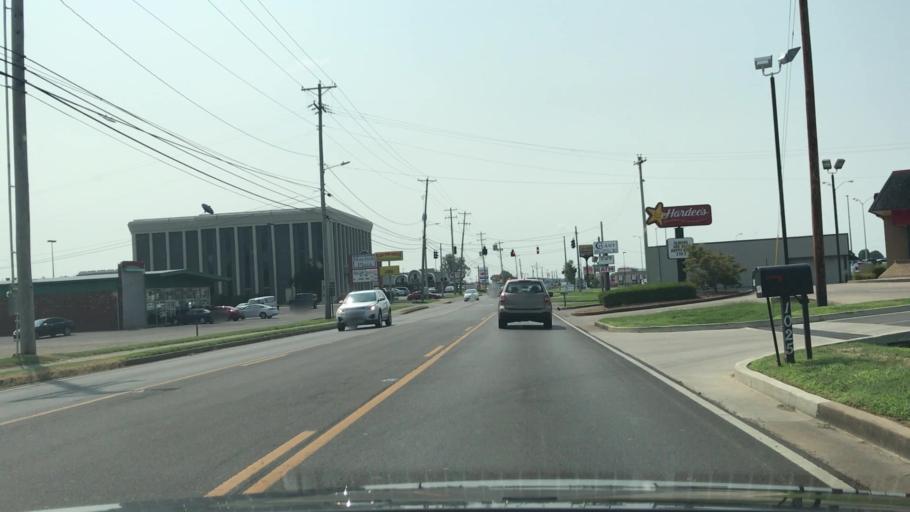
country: US
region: Kentucky
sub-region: Graves County
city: Mayfield
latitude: 36.7260
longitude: -88.6293
